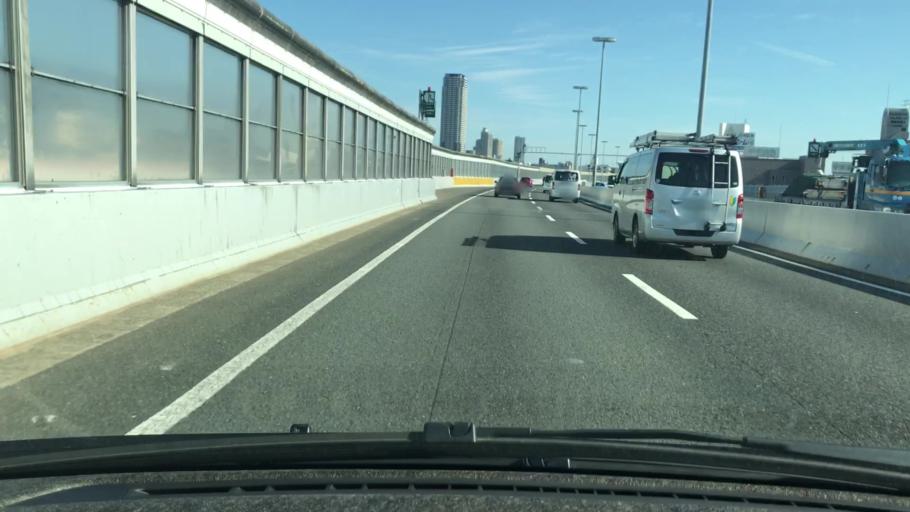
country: JP
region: Hyogo
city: Kobe
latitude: 34.7093
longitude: 135.2408
